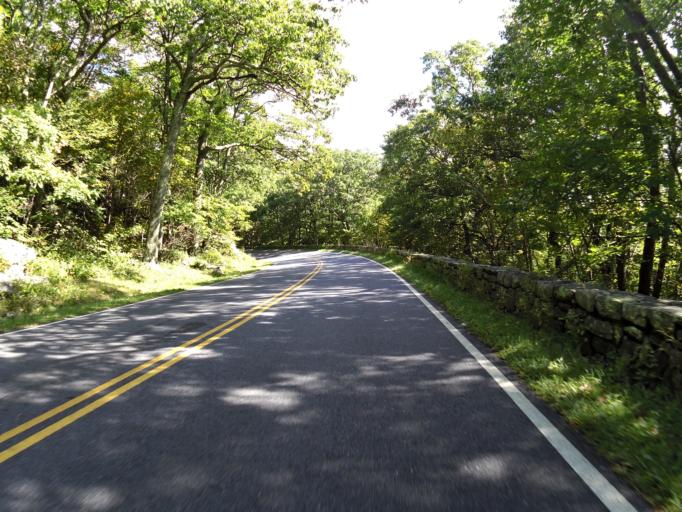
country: US
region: Virginia
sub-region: Page County
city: Stanley
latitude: 38.5569
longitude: -78.3808
